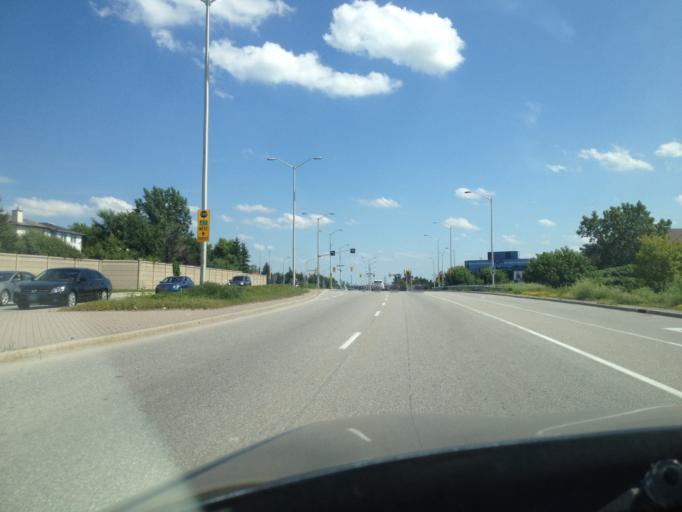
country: CA
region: Ontario
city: Bells Corners
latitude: 45.3034
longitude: -75.9093
